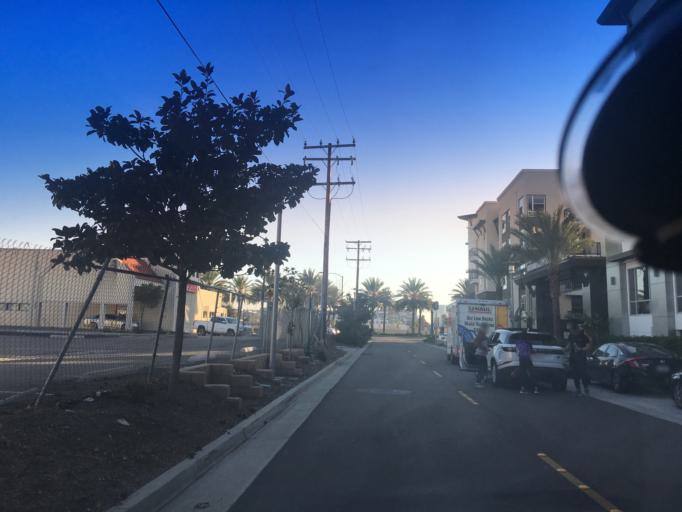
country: US
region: California
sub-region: Orange County
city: Anaheim
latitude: 33.8046
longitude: -117.8916
